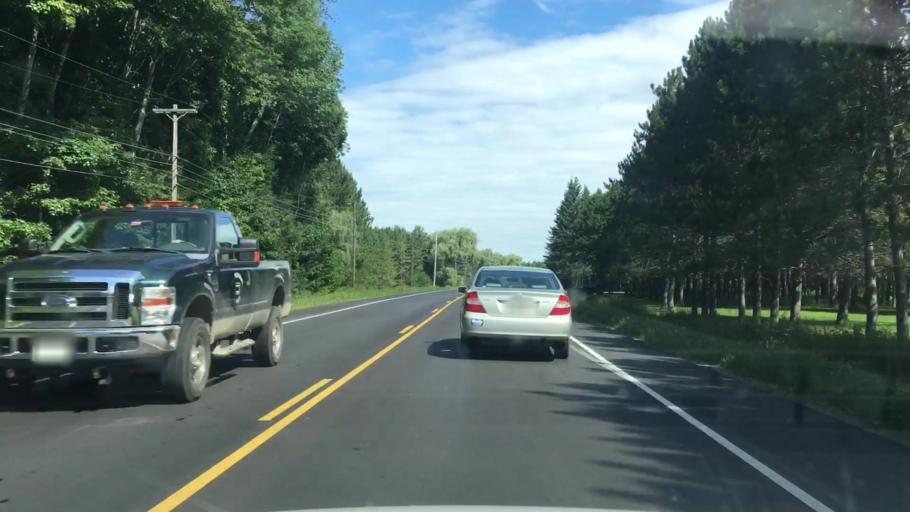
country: US
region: Maine
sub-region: Penobscot County
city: Corinna
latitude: 44.9412
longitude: -69.2479
